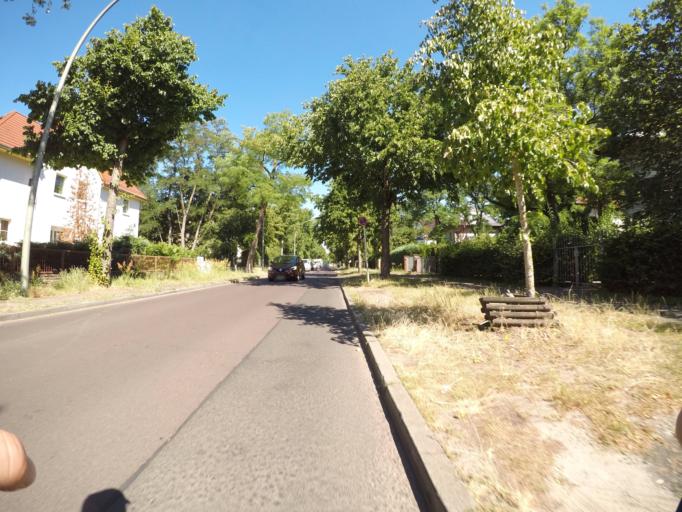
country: DE
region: Berlin
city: Karlshorst
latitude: 52.4851
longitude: 13.5313
